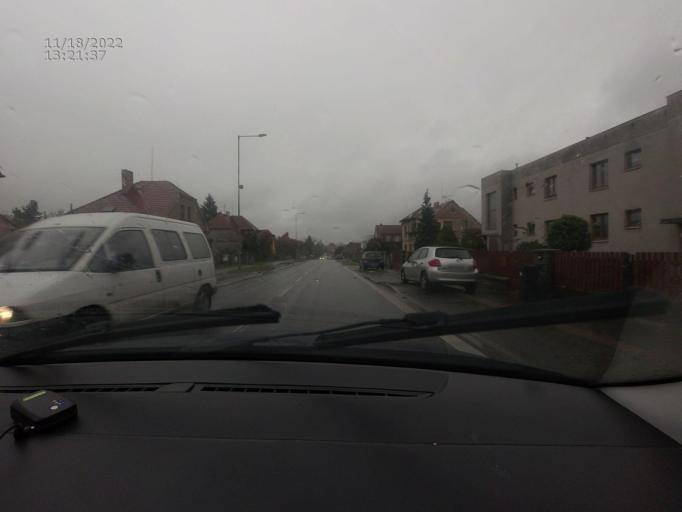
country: CZ
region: Plzensky
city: Horazd'ovice
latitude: 49.3246
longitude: 13.6885
